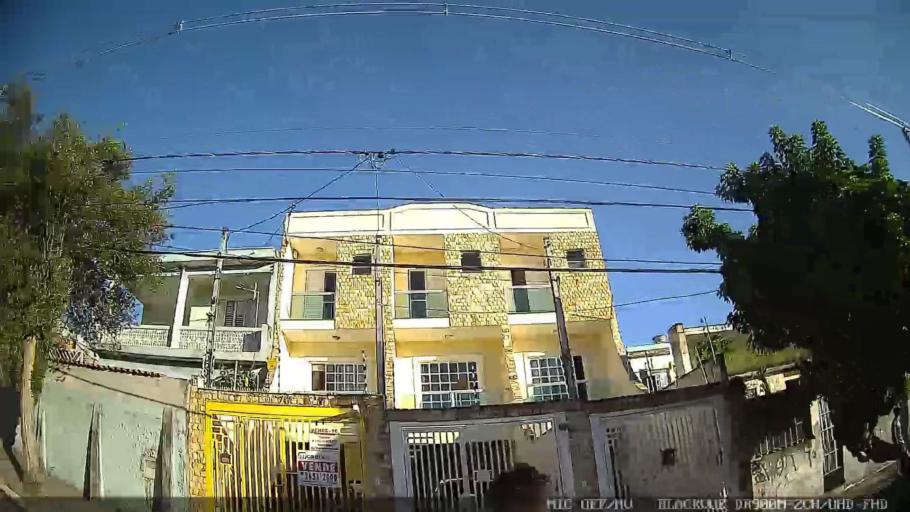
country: BR
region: Sao Paulo
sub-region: Guarulhos
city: Guarulhos
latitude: -23.5403
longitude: -46.5039
